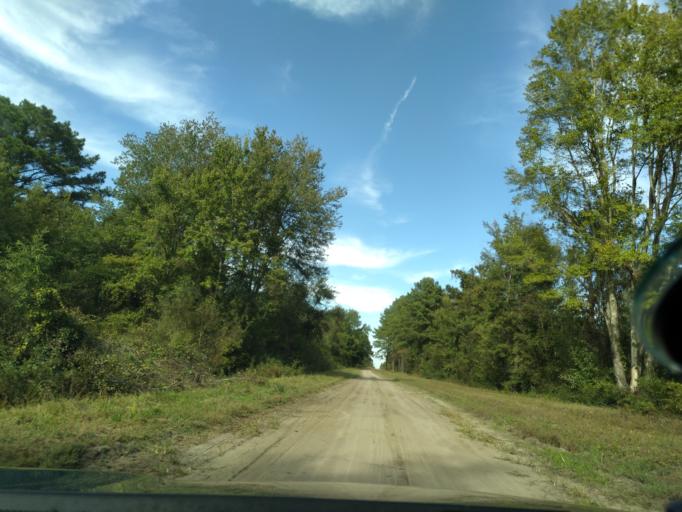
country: US
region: North Carolina
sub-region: Beaufort County
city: Belhaven
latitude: 35.7271
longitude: -76.5765
